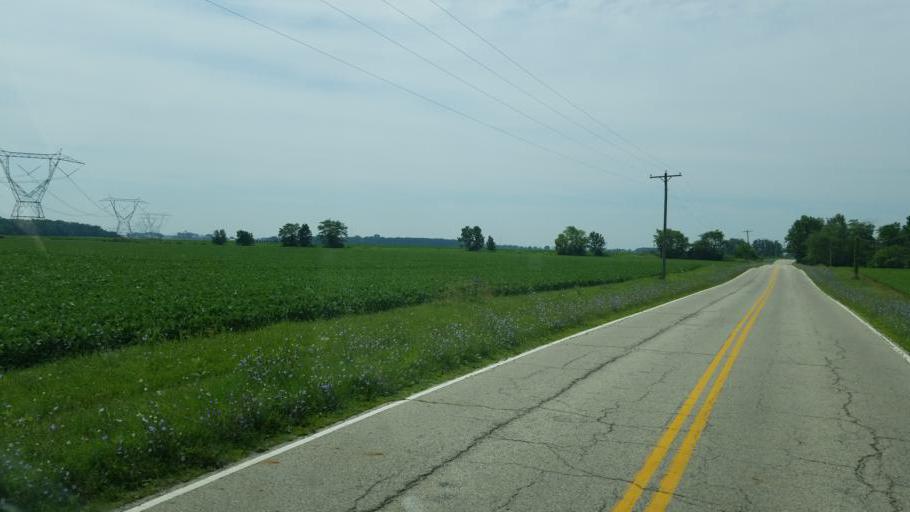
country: US
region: Ohio
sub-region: Madison County
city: Choctaw Lake
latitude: 39.9857
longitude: -83.3893
